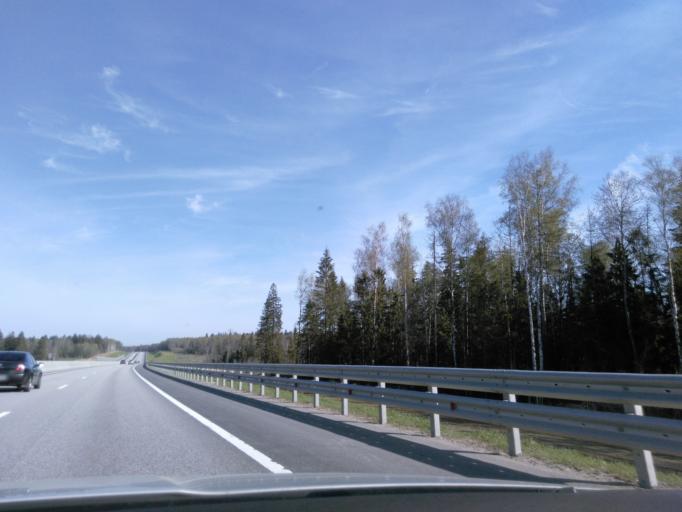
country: RU
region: Moskovskaya
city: Lozhki
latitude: 56.1184
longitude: 37.1160
